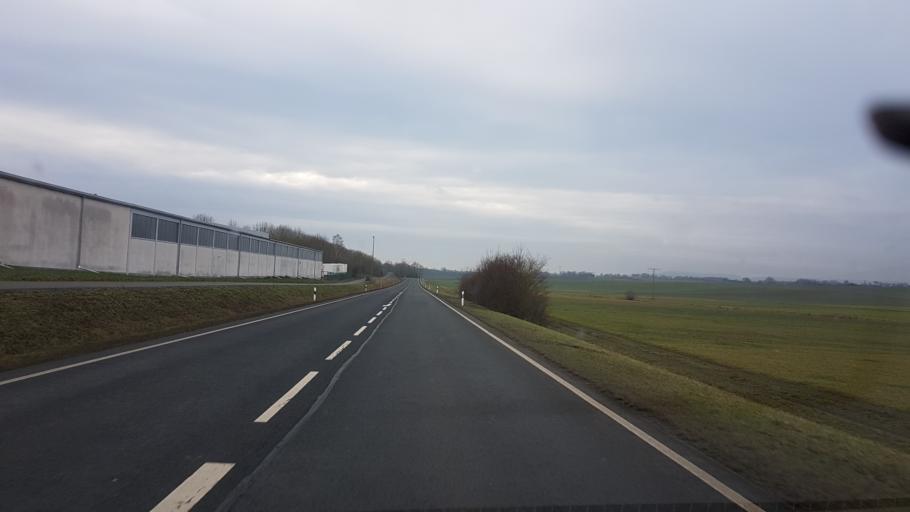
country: DE
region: Bavaria
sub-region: Regierungsbezirk Unterfranken
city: Ermershausen
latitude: 50.2376
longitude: 10.5688
